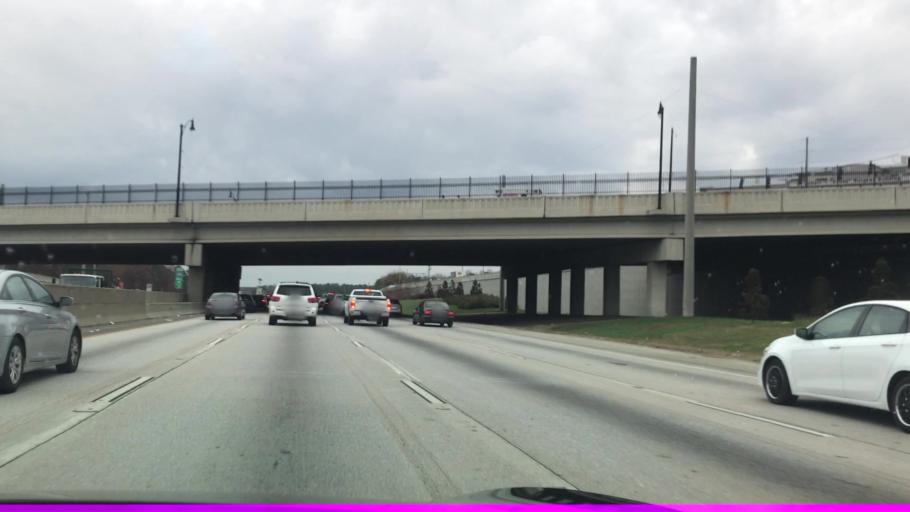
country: US
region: Georgia
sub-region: DeKalb County
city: Scottdale
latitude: 33.7787
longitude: -84.2422
